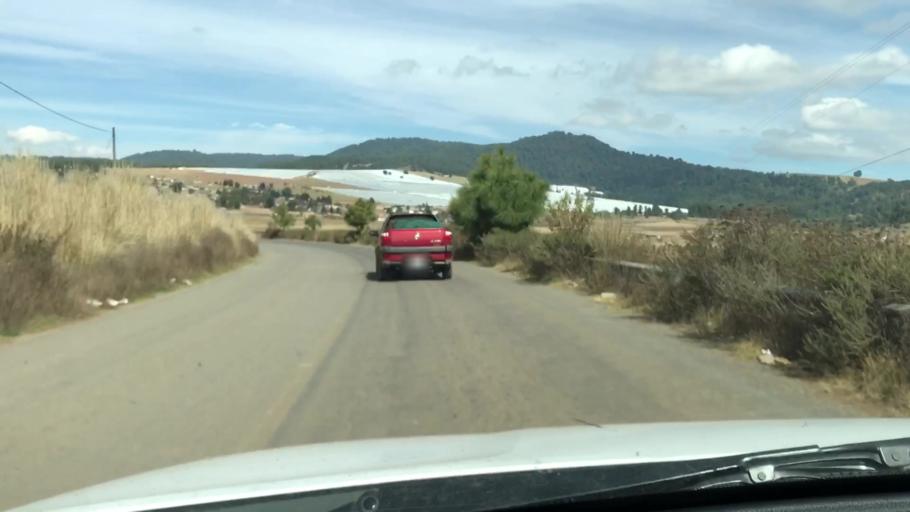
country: MX
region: Jalisco
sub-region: Amacueca
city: Tepec
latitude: 20.0208
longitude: -103.6885
